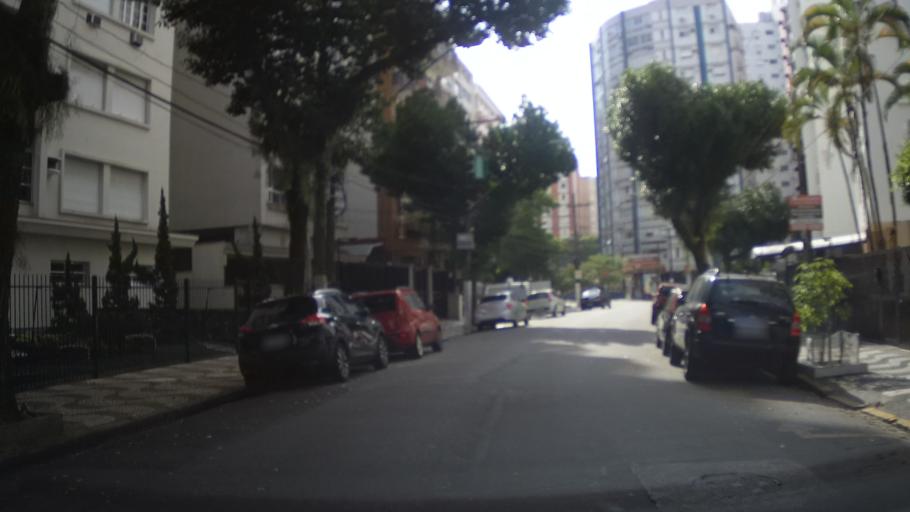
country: BR
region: Sao Paulo
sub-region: Santos
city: Santos
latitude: -23.9685
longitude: -46.3308
